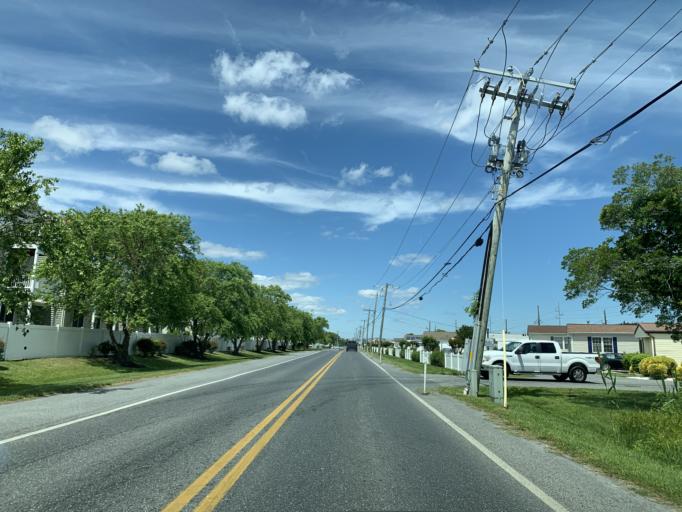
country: US
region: Maryland
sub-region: Worcester County
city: West Ocean City
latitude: 38.3322
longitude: -75.1064
